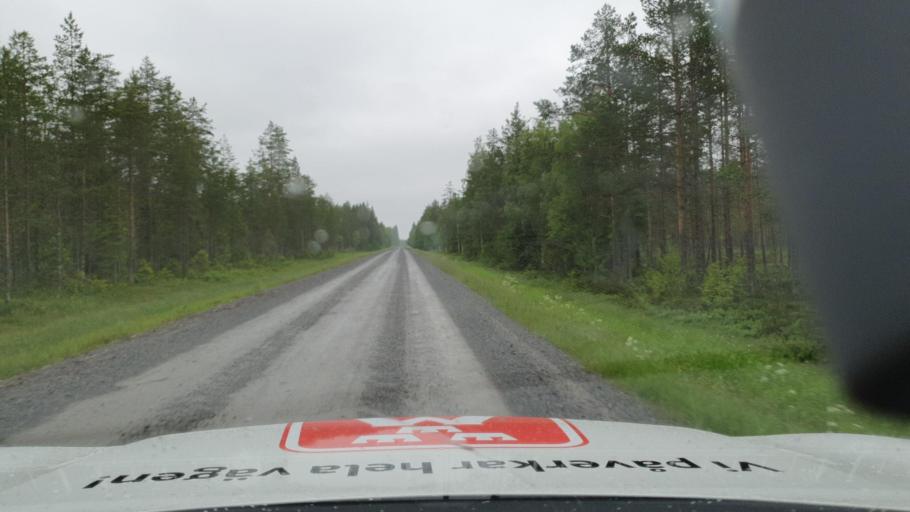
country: SE
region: Vaesterbotten
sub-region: Nordmalings Kommun
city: Nordmaling
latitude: 63.8234
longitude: 19.4924
